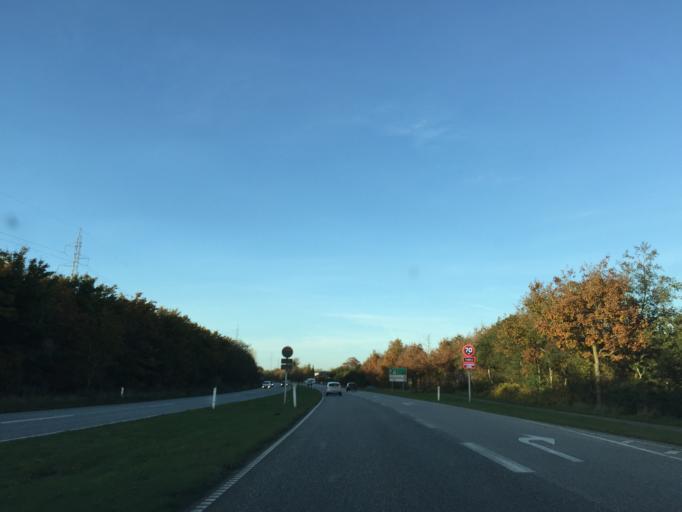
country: DK
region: South Denmark
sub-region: Aabenraa Kommune
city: Krusa
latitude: 54.8586
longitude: 9.4035
